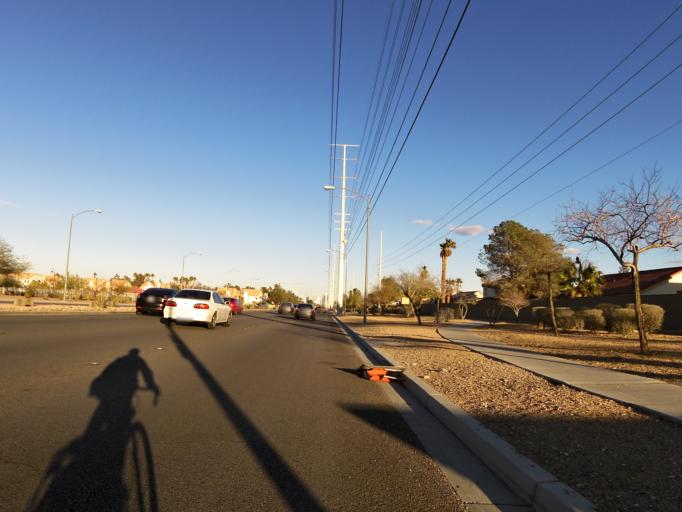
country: US
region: Nevada
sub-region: Clark County
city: Spring Valley
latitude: 36.1145
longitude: -115.2594
